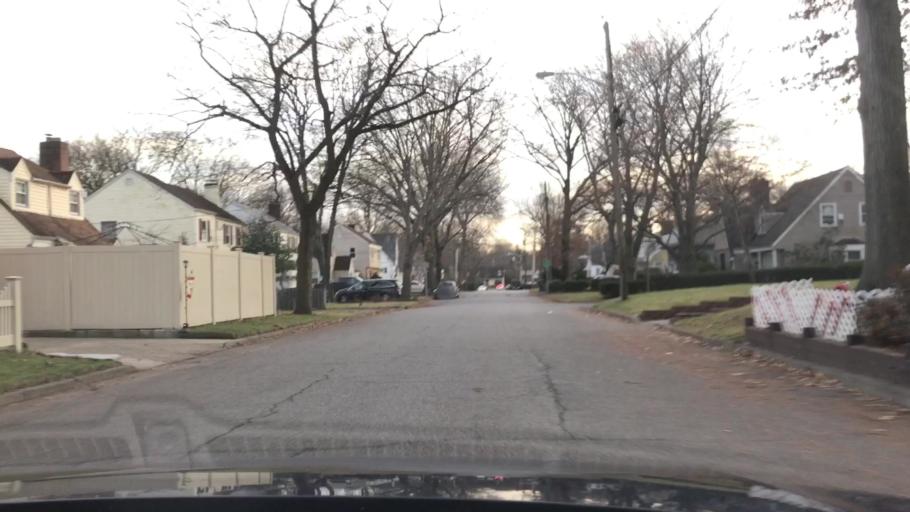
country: US
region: New Jersey
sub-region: Bergen County
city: Bergenfield
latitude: 40.9268
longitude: -73.9839
